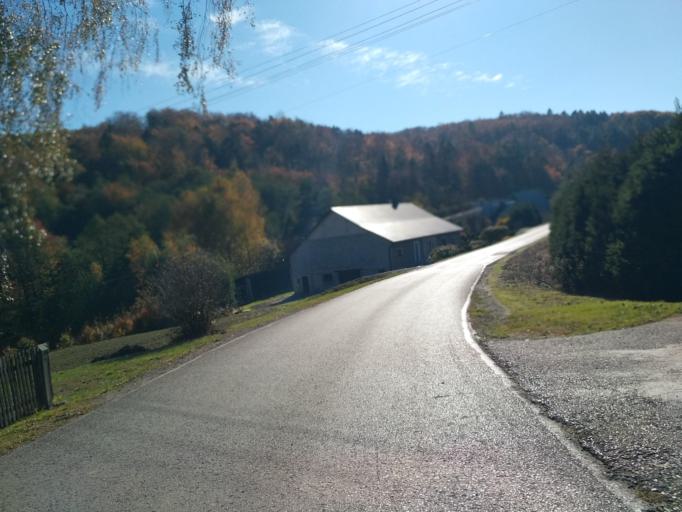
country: PL
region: Subcarpathian Voivodeship
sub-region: Powiat ropczycko-sedziszowski
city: Iwierzyce
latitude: 49.9771
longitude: 21.7289
